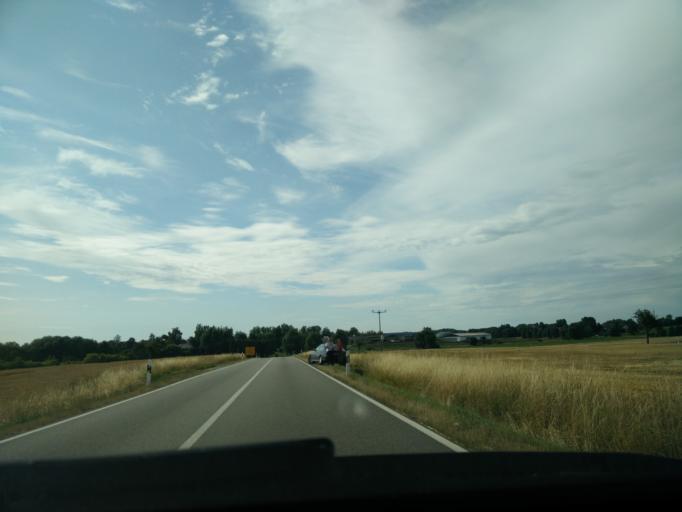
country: DE
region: Saxony
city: Bad Lausick
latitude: 51.1056
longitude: 12.6157
